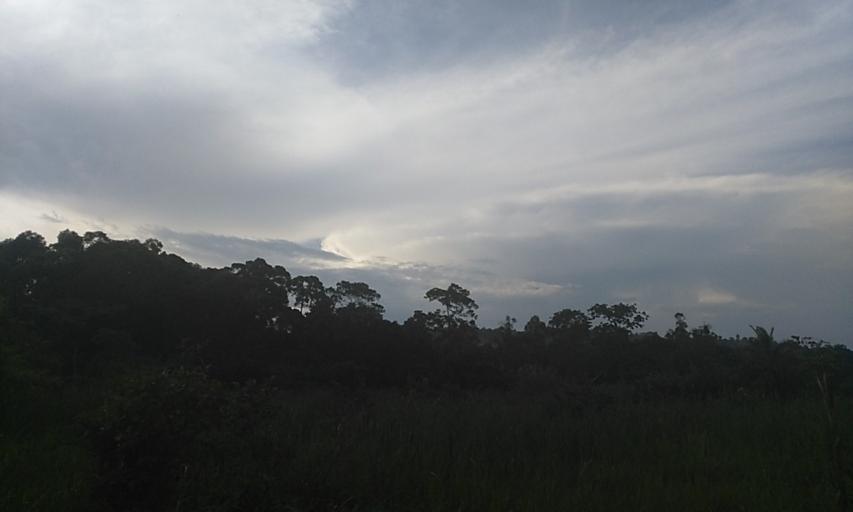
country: UG
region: Central Region
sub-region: Wakiso District
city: Kajansi
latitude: 0.2426
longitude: 32.4983
